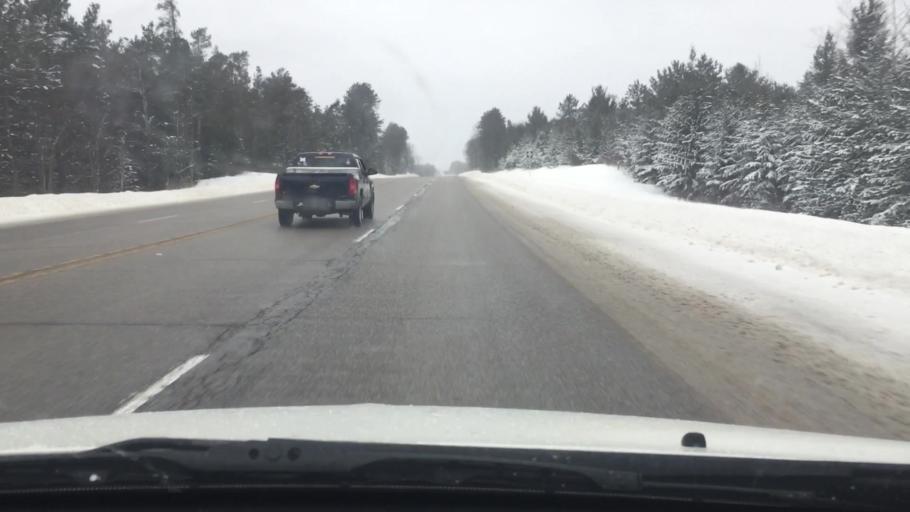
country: US
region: Michigan
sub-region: Otsego County
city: Gaylord
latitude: 45.0439
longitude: -84.7758
